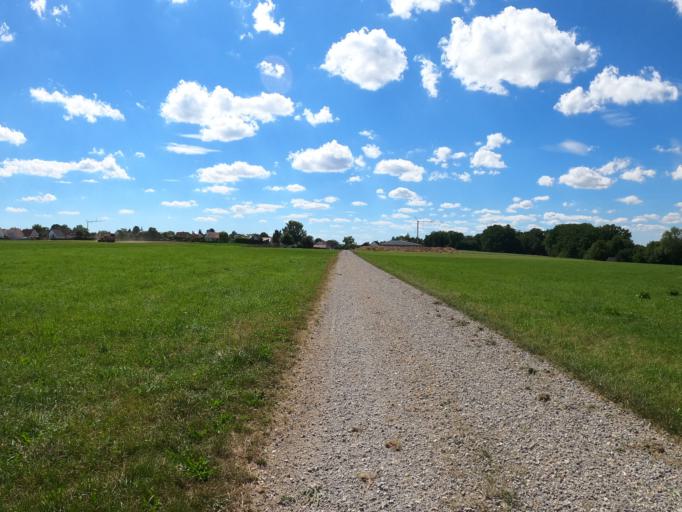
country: DE
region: Bavaria
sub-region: Swabia
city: Leipheim
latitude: 48.4217
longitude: 10.1967
